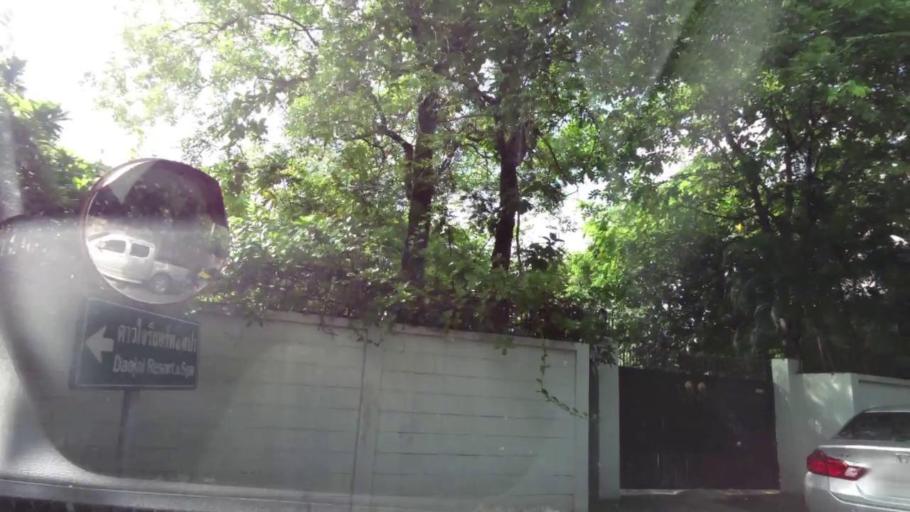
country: TH
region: Bangkok
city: Phra Khanong
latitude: 13.7176
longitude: 100.6010
